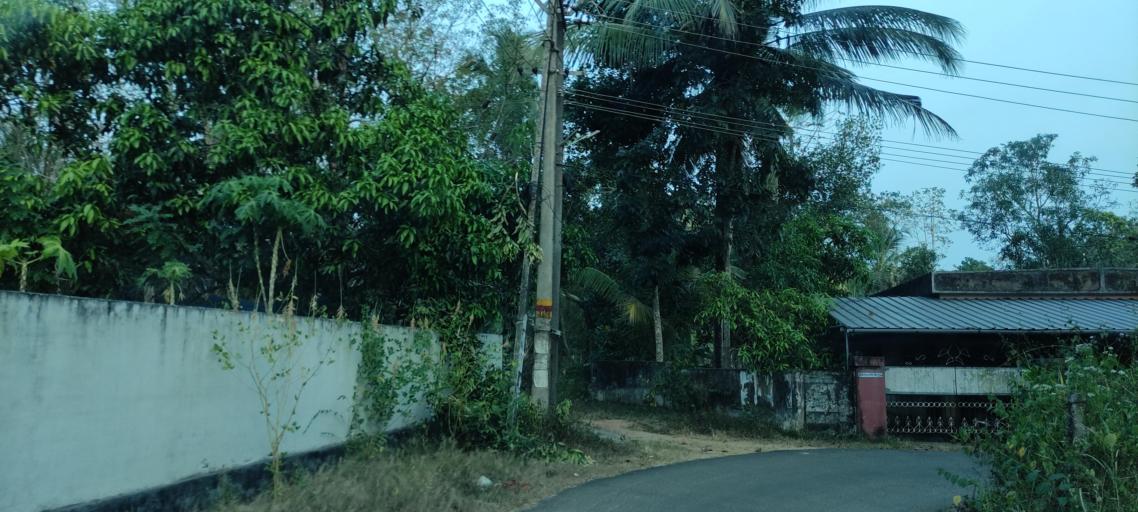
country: IN
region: Kerala
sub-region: Alappuzha
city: Mavelikara
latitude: 9.2784
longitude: 76.5514
